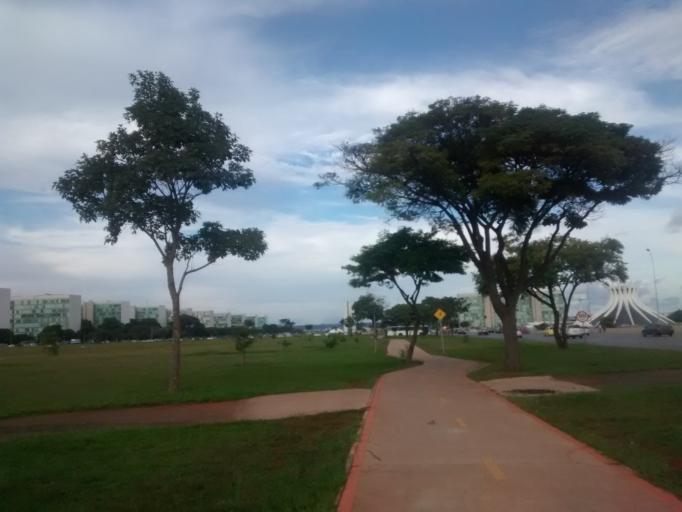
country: BR
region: Federal District
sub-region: Brasilia
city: Brasilia
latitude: -15.7959
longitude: -47.8789
